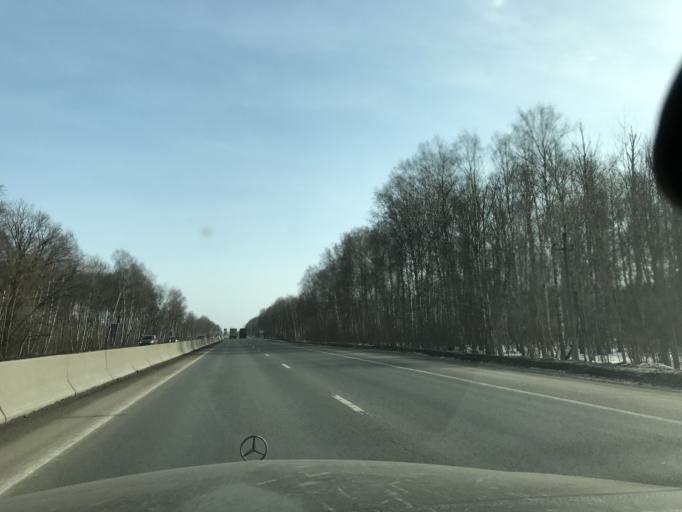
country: RU
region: Nizjnij Novgorod
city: Gorbatovka
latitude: 56.3078
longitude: 43.7160
